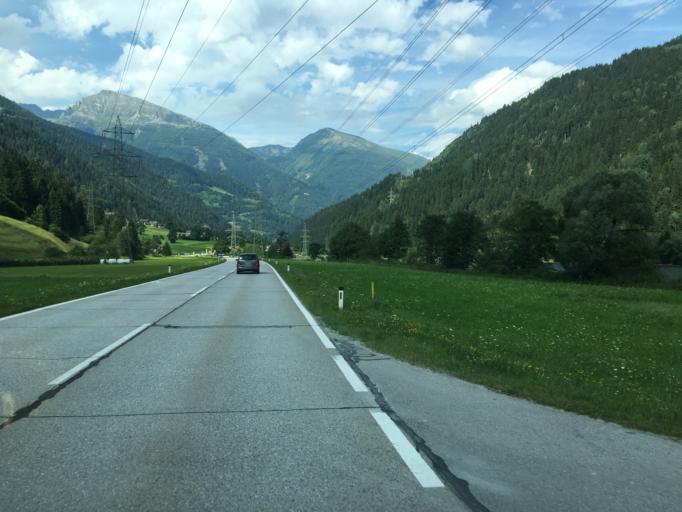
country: AT
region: Carinthia
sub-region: Politischer Bezirk Spittal an der Drau
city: Stall
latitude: 46.9106
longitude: 13.0677
